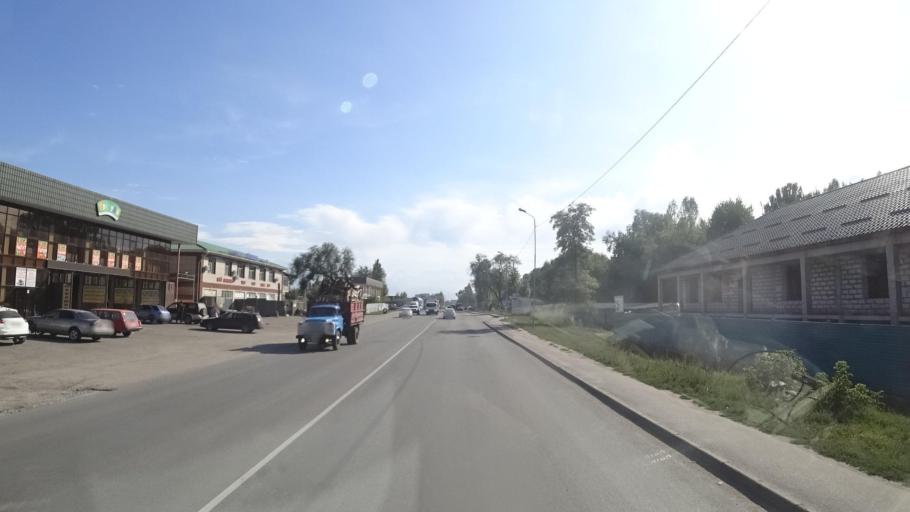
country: KZ
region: Almaty Oblysy
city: Energeticheskiy
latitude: 43.4223
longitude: 77.0234
